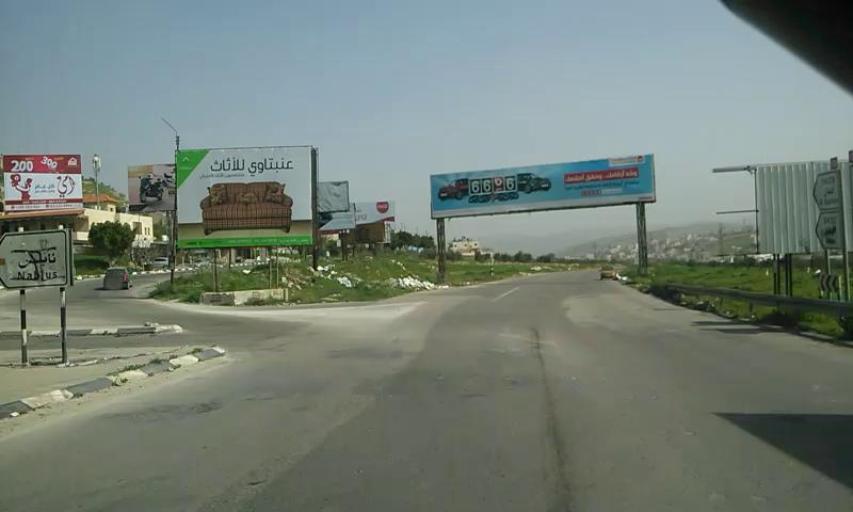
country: PS
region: West Bank
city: Kafr Qallil
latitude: 32.1822
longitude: 35.2766
